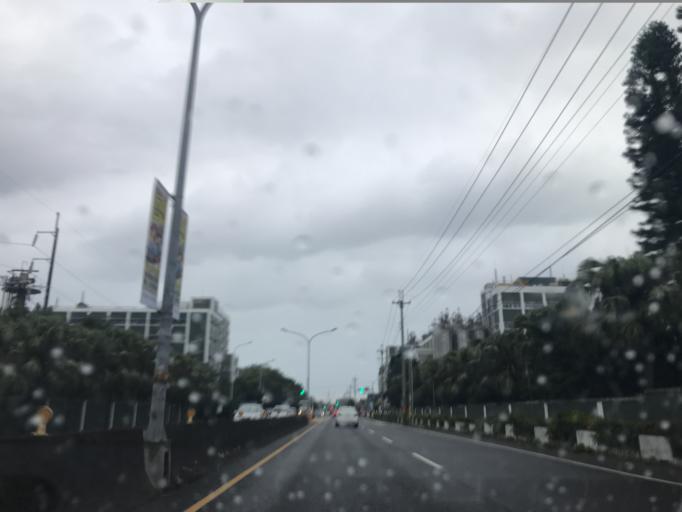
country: TW
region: Taiwan
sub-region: Hsinchu
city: Zhubei
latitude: 24.8251
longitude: 121.0588
